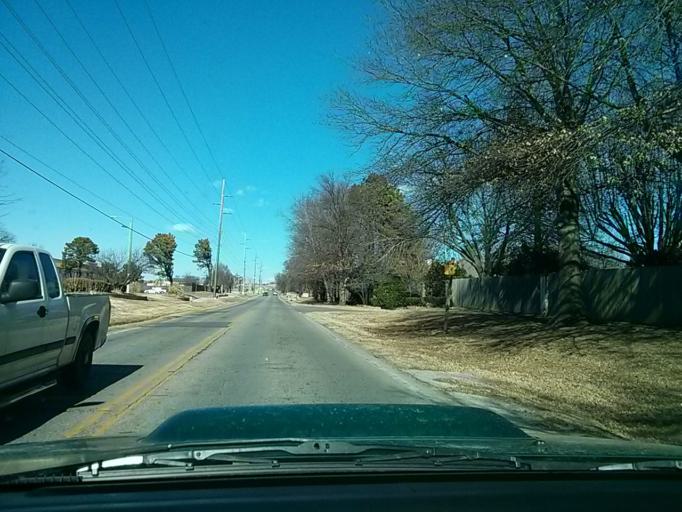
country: US
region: Oklahoma
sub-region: Tulsa County
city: Jenks
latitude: 36.0372
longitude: -95.9489
